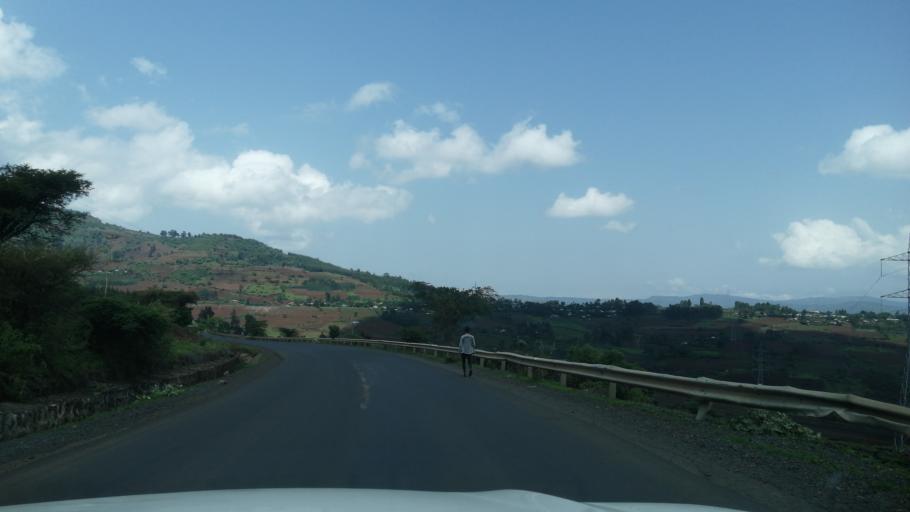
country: ET
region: Oromiya
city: Guder
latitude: 8.9877
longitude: 37.6079
